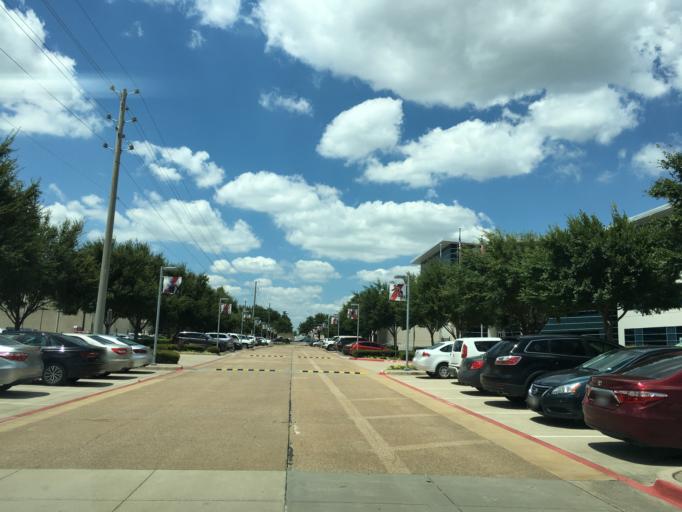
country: US
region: Texas
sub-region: Dallas County
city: Addison
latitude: 32.9484
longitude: -96.8341
